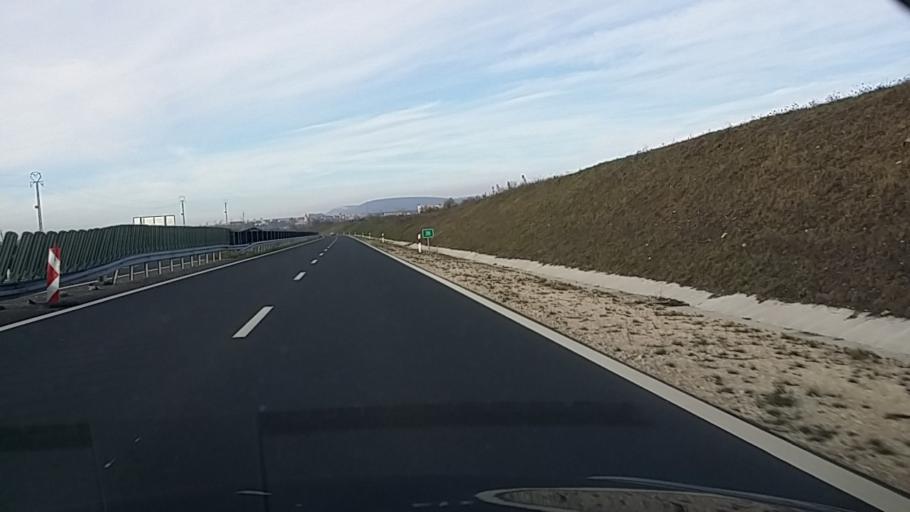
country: HU
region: Veszprem
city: Varpalota
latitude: 47.1963
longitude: 18.1708
